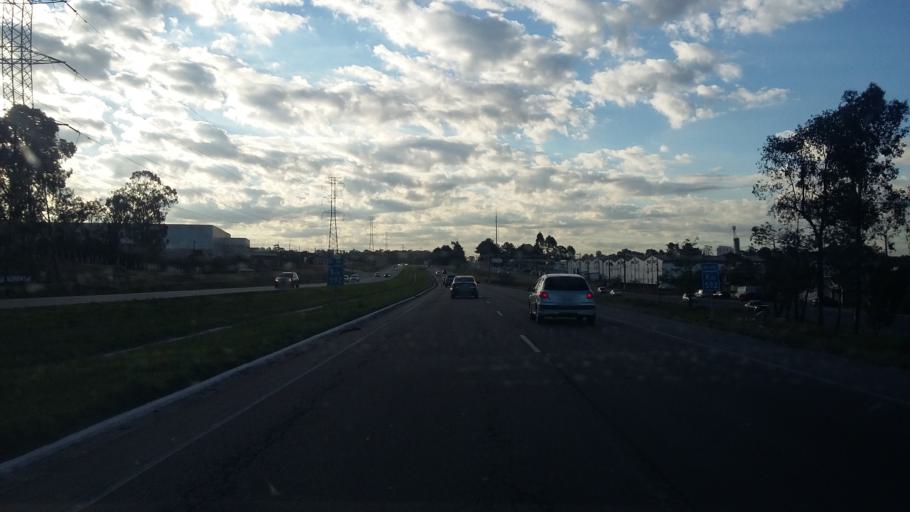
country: BR
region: Parana
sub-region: Curitiba
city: Curitiba
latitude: -25.4754
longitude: -49.3514
